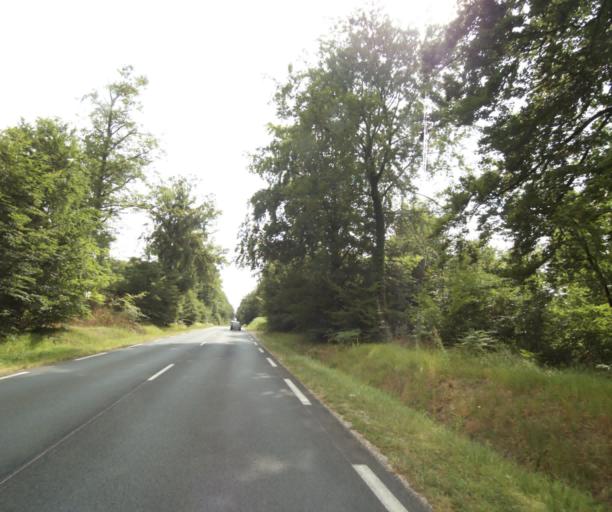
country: FR
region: Ile-de-France
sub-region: Departement de Seine-et-Marne
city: Acheres-la-Foret
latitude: 48.3668
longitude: 2.6349
